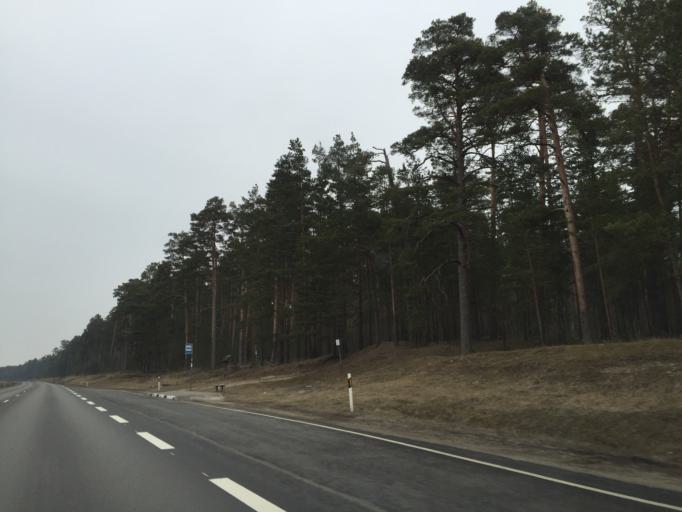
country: EE
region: Paernumaa
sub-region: Paernu linn
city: Parnu
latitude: 58.1839
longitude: 24.4925
